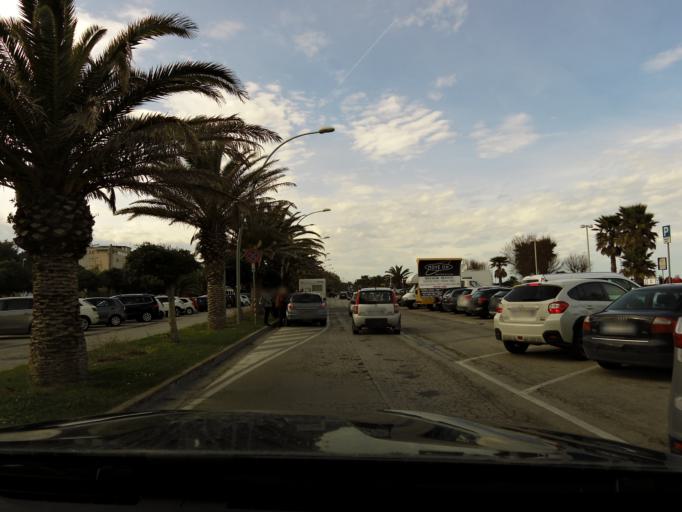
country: IT
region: The Marches
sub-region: Provincia di Macerata
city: Portocivitanova
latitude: 43.3033
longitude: 13.7364
